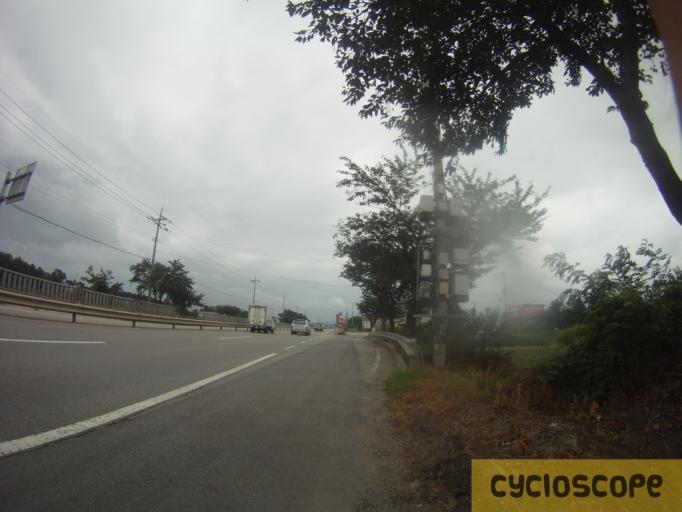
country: KR
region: Gyeonggi-do
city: Hwaseong-si
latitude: 37.0204
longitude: 126.8098
